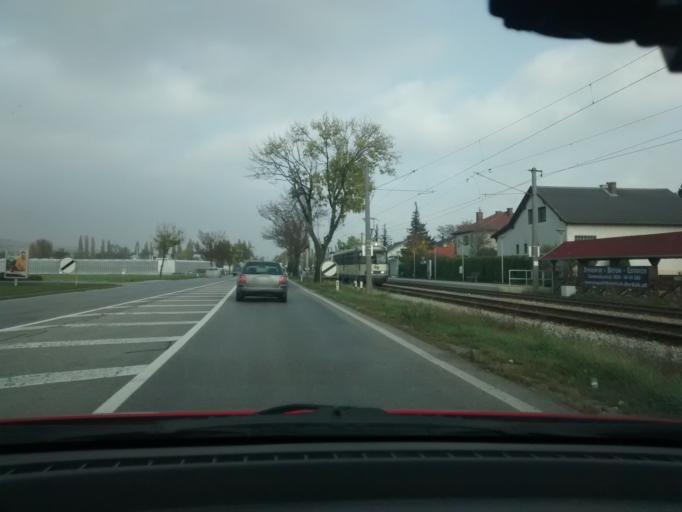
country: AT
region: Lower Austria
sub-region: Politischer Bezirk Modling
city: Guntramsdorf
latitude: 48.0387
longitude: 16.3037
